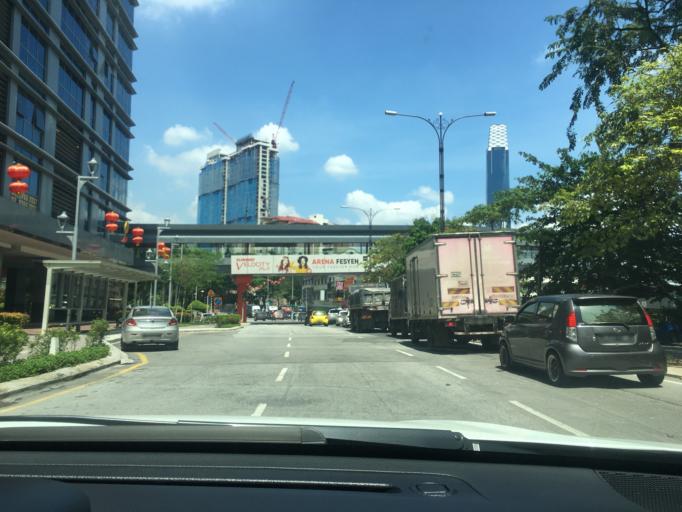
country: MY
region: Kuala Lumpur
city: Kuala Lumpur
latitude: 3.1302
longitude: 101.7234
